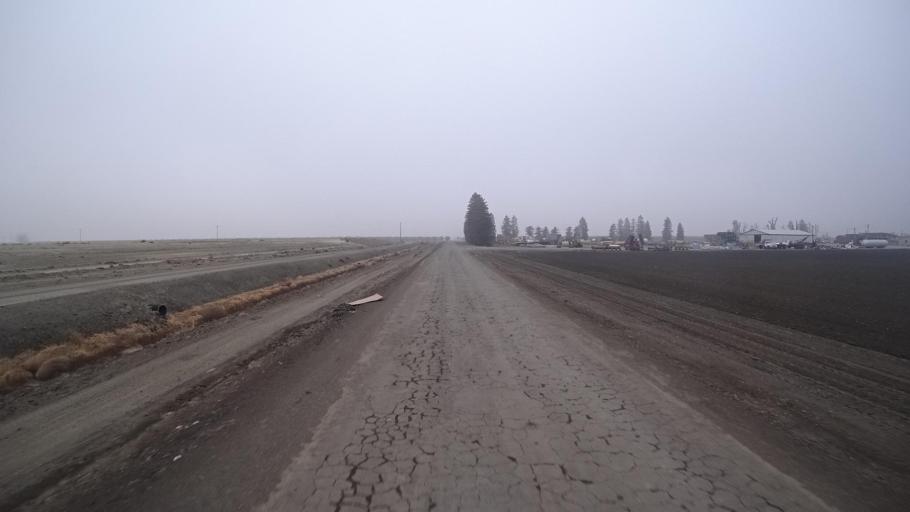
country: US
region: California
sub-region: Kern County
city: Buttonwillow
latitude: 35.4124
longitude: -119.5163
